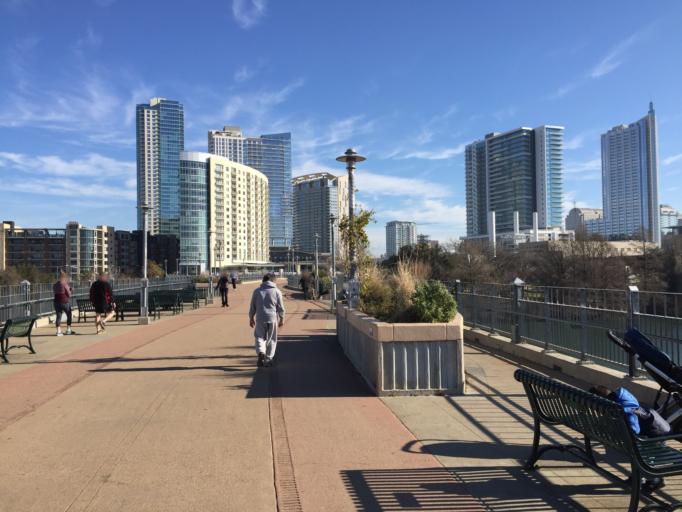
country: US
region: Texas
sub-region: Travis County
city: Austin
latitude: 30.2652
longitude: -97.7561
